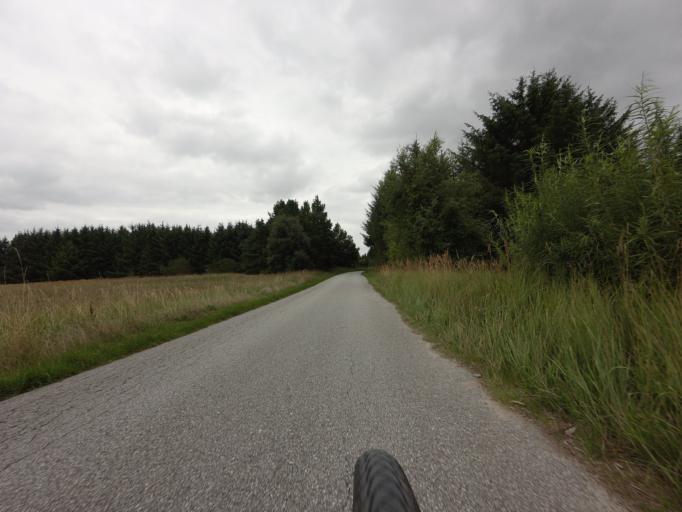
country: DK
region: North Denmark
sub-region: Hjorring Kommune
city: Hirtshals
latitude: 57.5825
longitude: 10.0362
